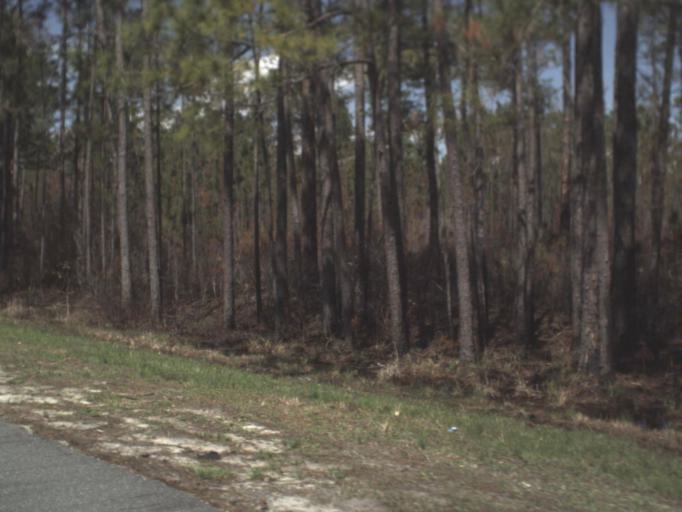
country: US
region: Florida
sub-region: Gadsden County
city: Midway
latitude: 30.3808
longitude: -84.5642
